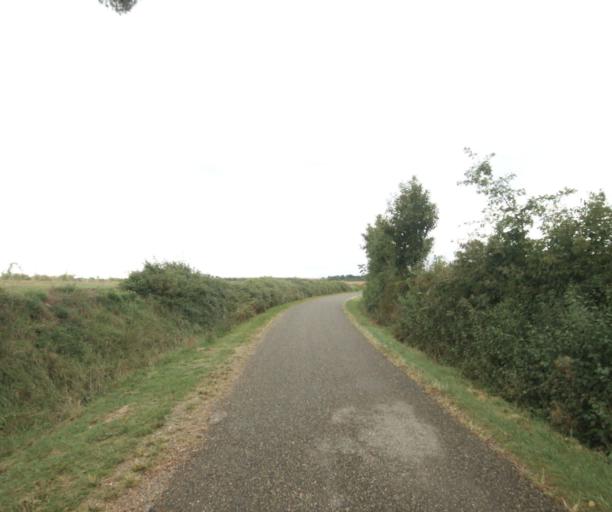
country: FR
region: Midi-Pyrenees
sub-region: Departement du Gers
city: Cazaubon
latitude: 43.8976
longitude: -0.1552
